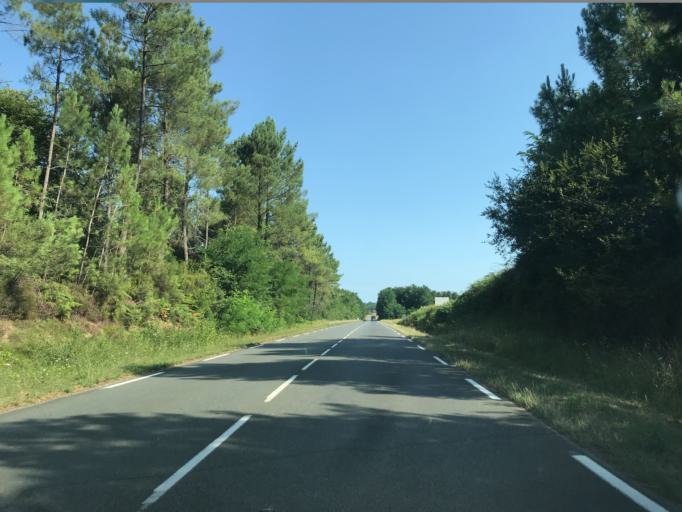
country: FR
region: Aquitaine
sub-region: Departement de la Dordogne
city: Sarlat-la-Caneda
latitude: 44.9663
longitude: 1.2376
